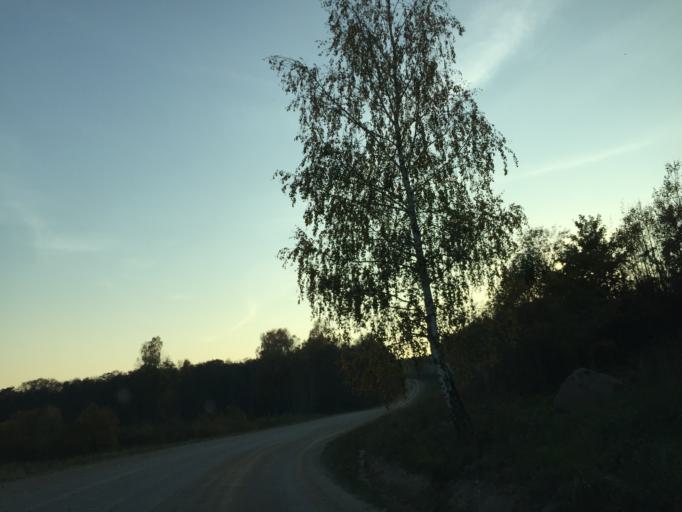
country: LV
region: Vainode
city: Vainode
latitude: 56.5055
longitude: 21.8154
